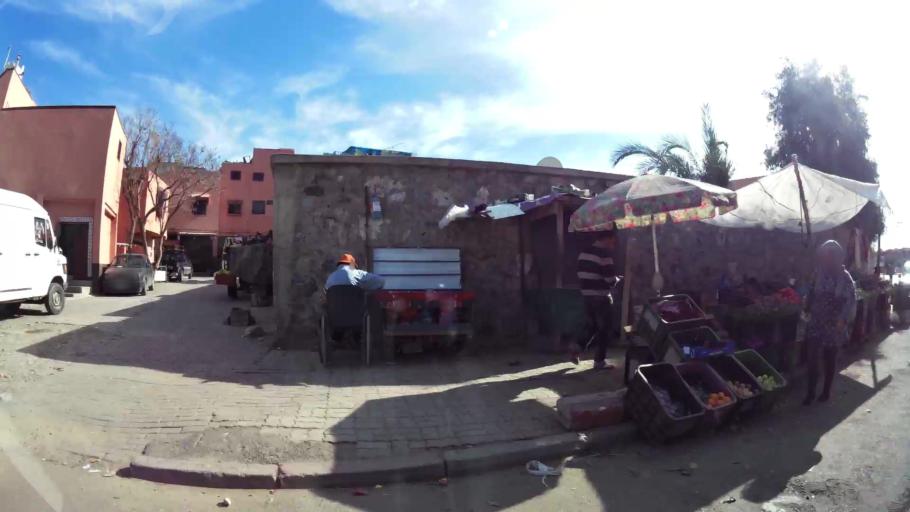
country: MA
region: Marrakech-Tensift-Al Haouz
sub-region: Marrakech
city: Marrakesh
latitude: 31.6531
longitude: -8.0302
